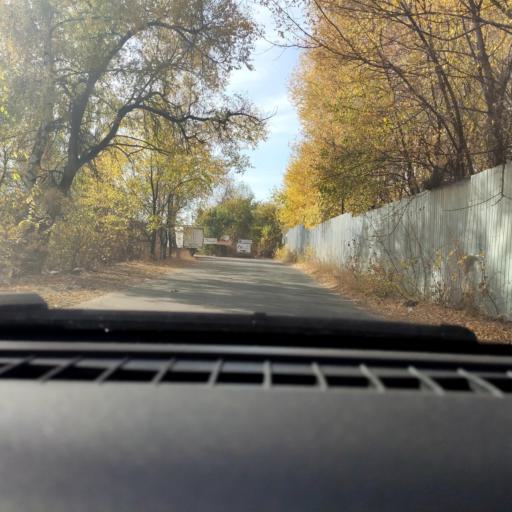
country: RU
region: Voronezj
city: Somovo
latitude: 51.6838
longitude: 39.2987
